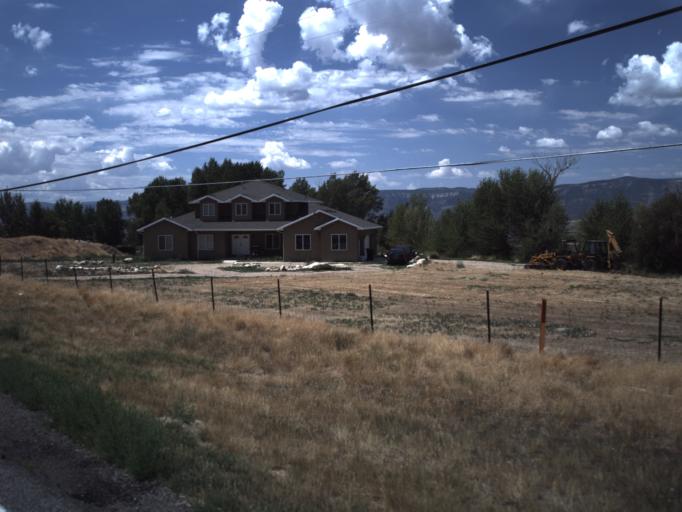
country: US
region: Utah
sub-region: Sanpete County
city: Mount Pleasant
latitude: 39.5187
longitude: -111.4749
